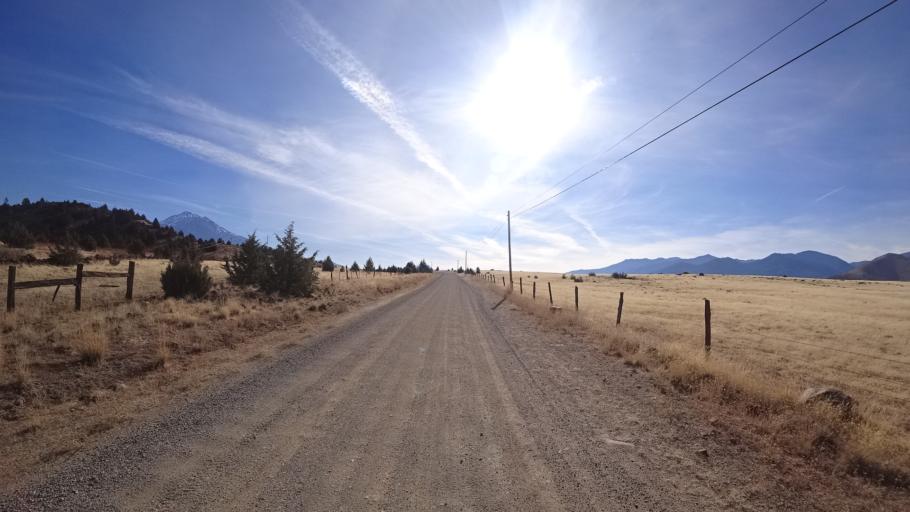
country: US
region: California
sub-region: Siskiyou County
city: Weed
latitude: 41.4931
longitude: -122.4517
